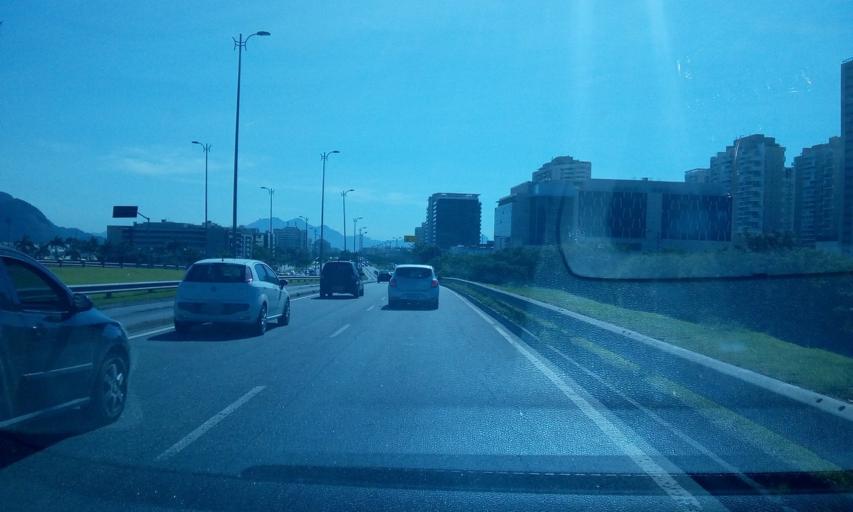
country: BR
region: Rio de Janeiro
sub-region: Nilopolis
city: Nilopolis
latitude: -23.0209
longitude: -43.4921
